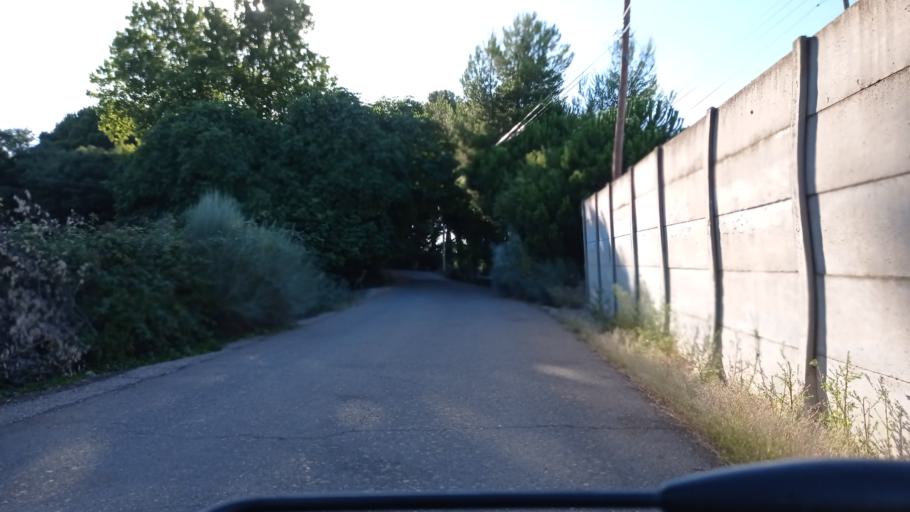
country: ES
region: Aragon
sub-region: Provincia de Zaragoza
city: Oliver-Valdefierro, Oliver, Valdefierro
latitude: 41.6639
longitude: -0.9525
